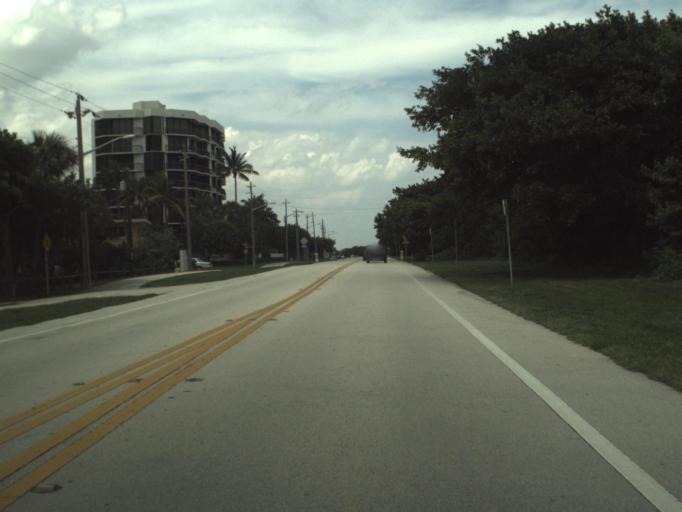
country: US
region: Florida
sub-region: Palm Beach County
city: Boca Raton
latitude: 26.3713
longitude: -80.0684
